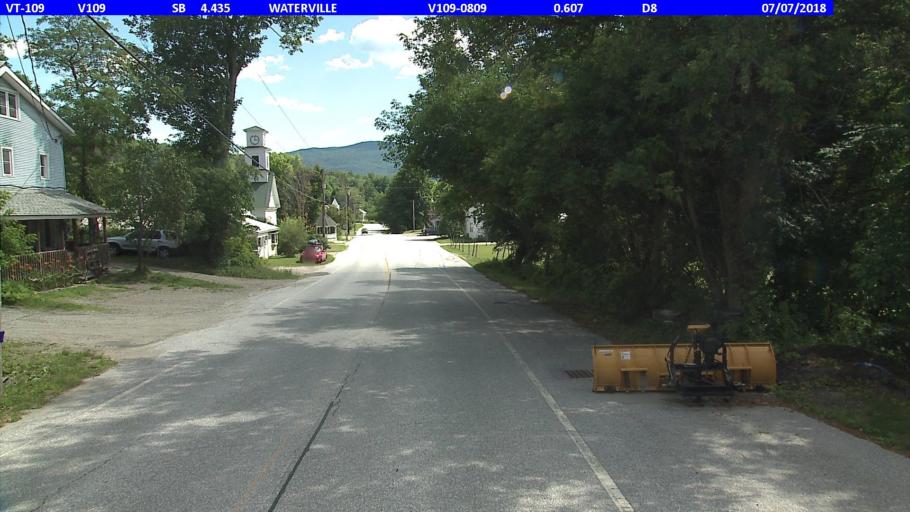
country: US
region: Vermont
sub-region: Lamoille County
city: Johnson
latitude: 44.6913
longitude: -72.7693
